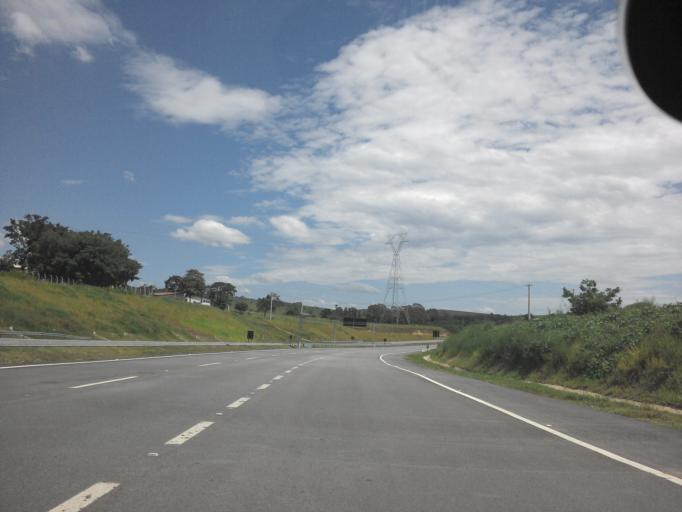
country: BR
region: Sao Paulo
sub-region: Taubate
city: Taubate
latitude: -23.0855
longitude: -45.5481
